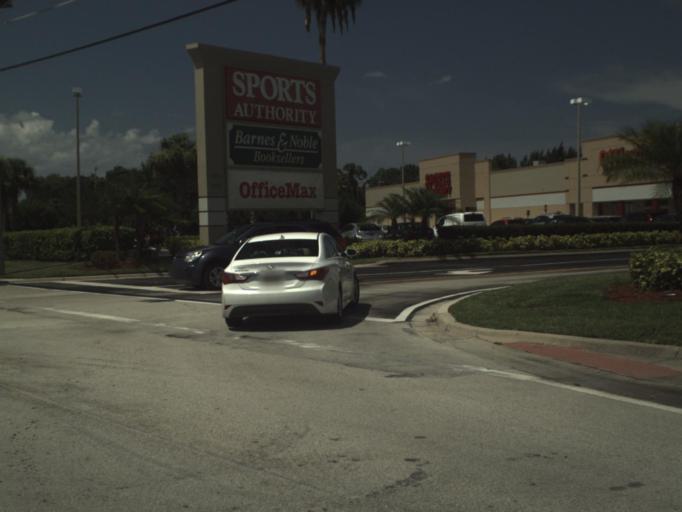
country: US
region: Florida
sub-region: Martin County
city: North River Shores
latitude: 27.2407
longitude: -80.2703
